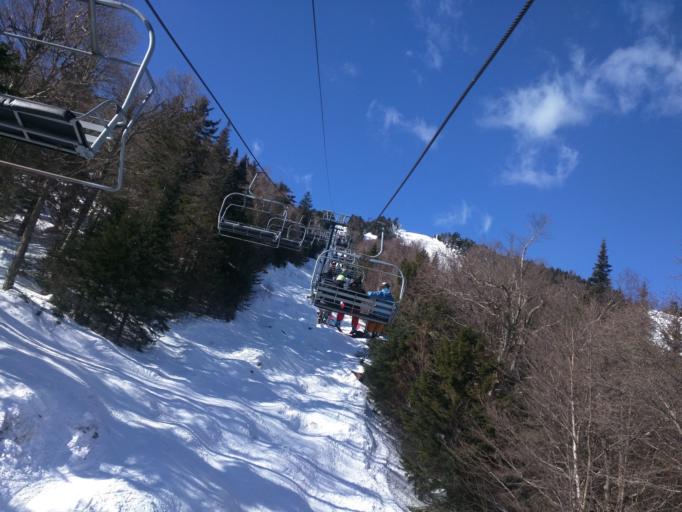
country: US
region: New York
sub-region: Warren County
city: Warrensburg
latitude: 43.6713
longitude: -74.0410
